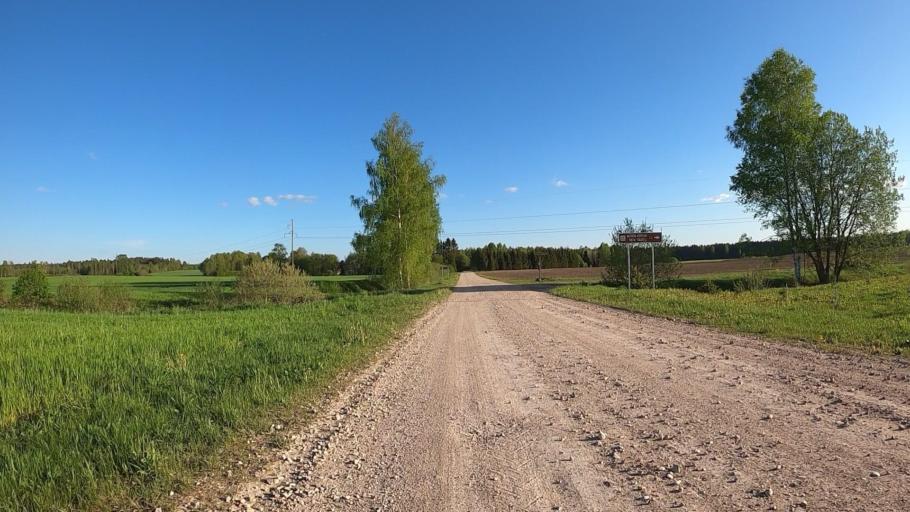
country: LV
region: Kekava
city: Kekava
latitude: 56.7702
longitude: 24.2876
